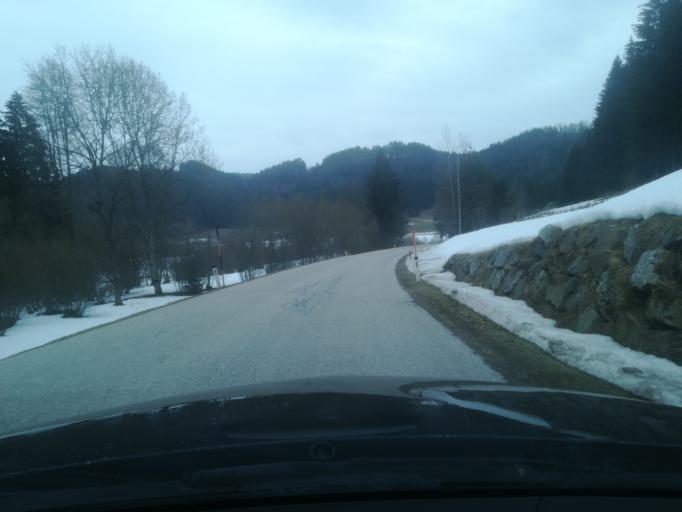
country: AT
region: Upper Austria
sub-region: Politischer Bezirk Perg
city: Perg
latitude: 48.3868
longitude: 14.6297
